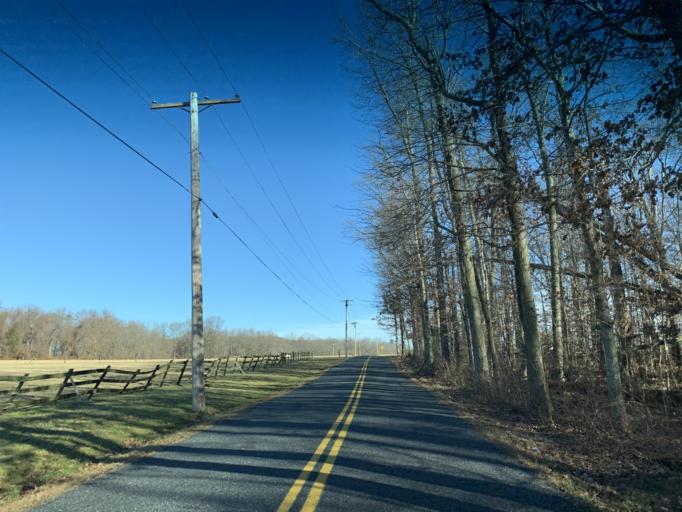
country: US
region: Maryland
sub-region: Harford County
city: Riverside
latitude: 39.5354
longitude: -76.2436
